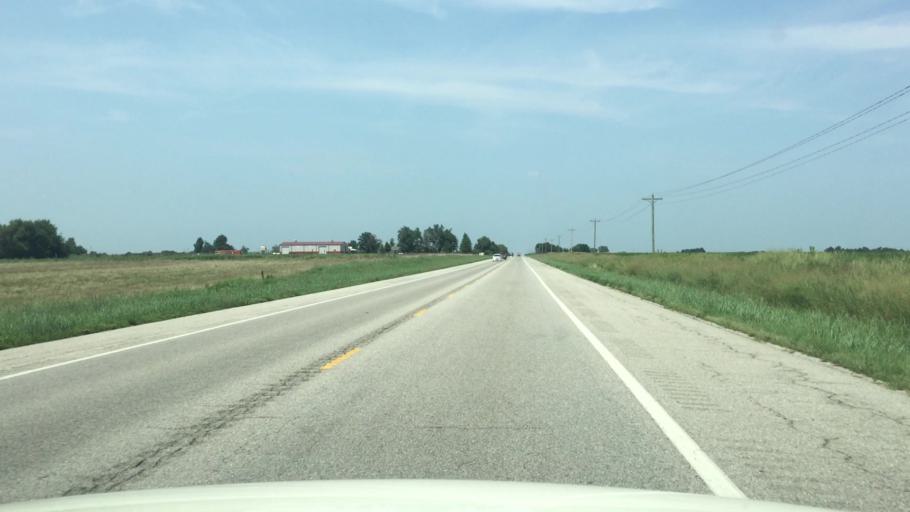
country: US
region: Kansas
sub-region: Crawford County
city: Pittsburg
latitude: 37.2676
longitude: -94.7052
